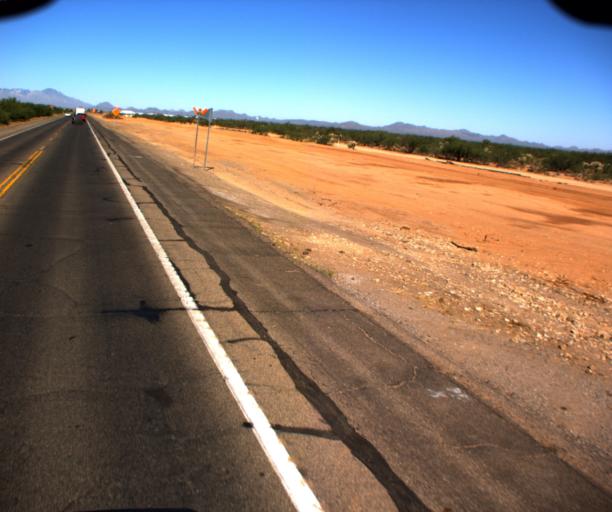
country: US
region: Arizona
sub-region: Pima County
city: Valencia West
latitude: 32.1412
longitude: -111.1489
